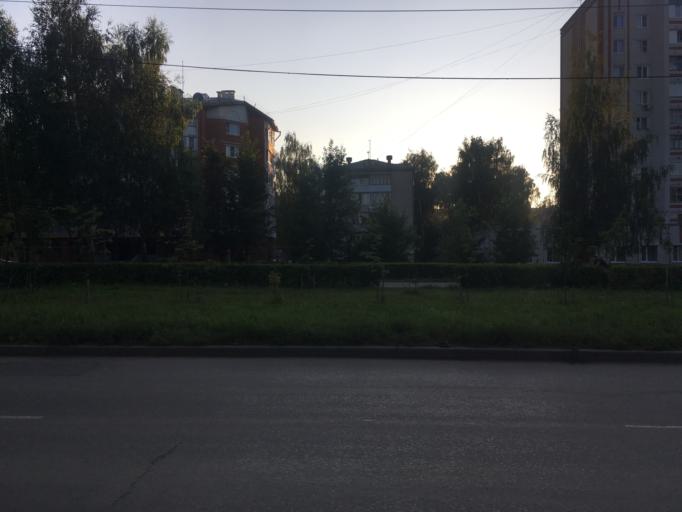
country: RU
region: Mariy-El
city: Yoshkar-Ola
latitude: 56.6498
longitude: 47.8748
